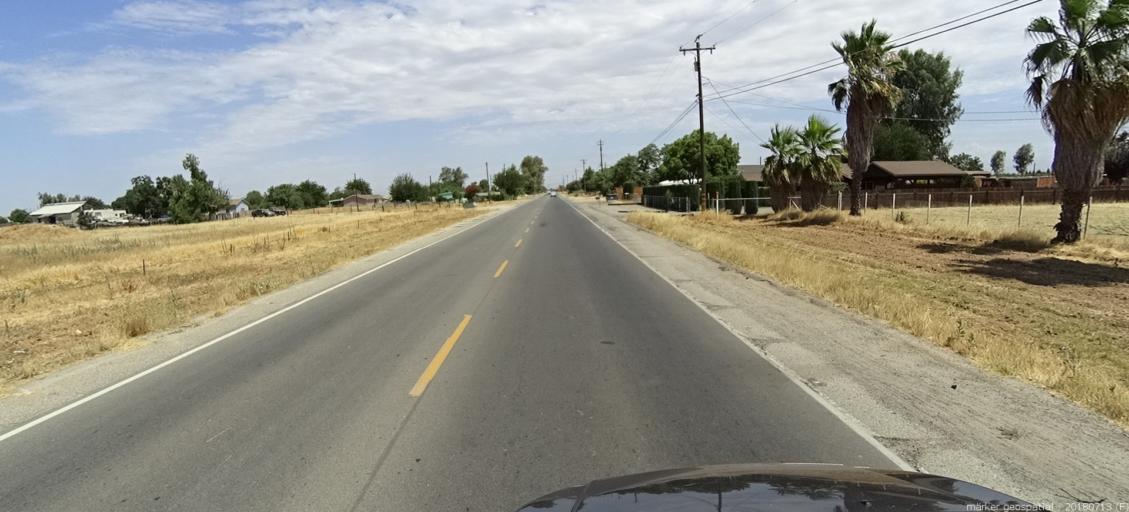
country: US
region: California
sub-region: Madera County
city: Madera
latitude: 36.9892
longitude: -120.0562
